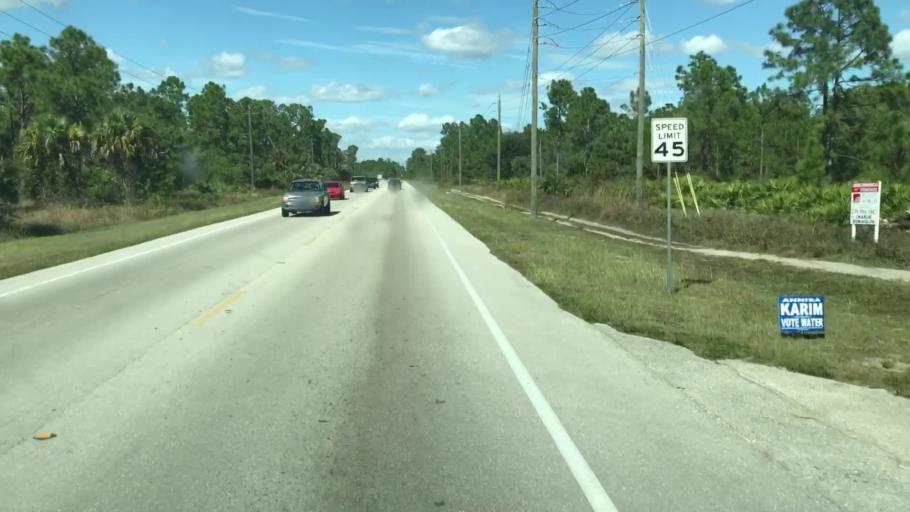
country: US
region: Florida
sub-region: Lee County
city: Alva
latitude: 26.6839
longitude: -81.5985
